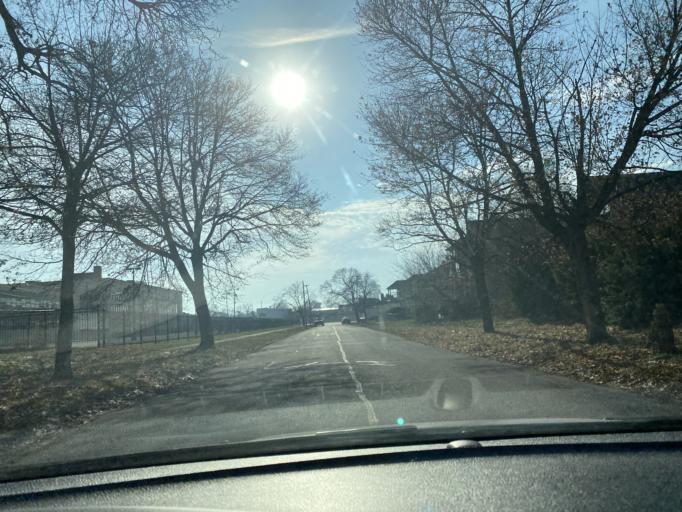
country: US
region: Michigan
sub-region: Wayne County
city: Highland Park
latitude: 42.3722
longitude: -83.1433
